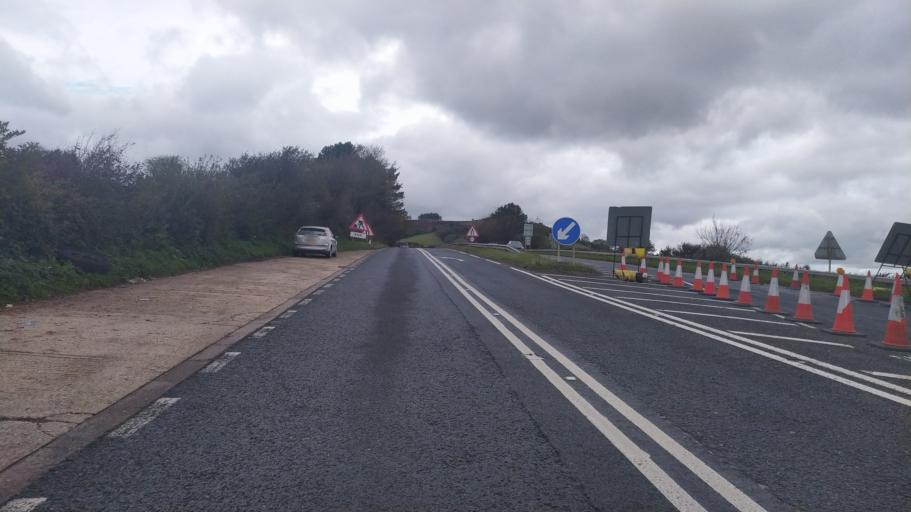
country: GB
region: England
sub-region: Dorset
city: Bridport
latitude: 50.7378
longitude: -2.8348
